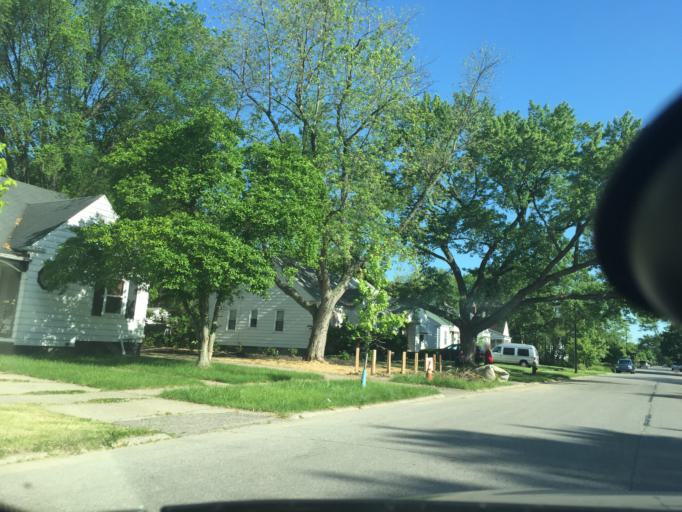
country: US
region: Michigan
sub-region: Oakland County
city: Southfield
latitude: 42.4139
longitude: -83.2266
